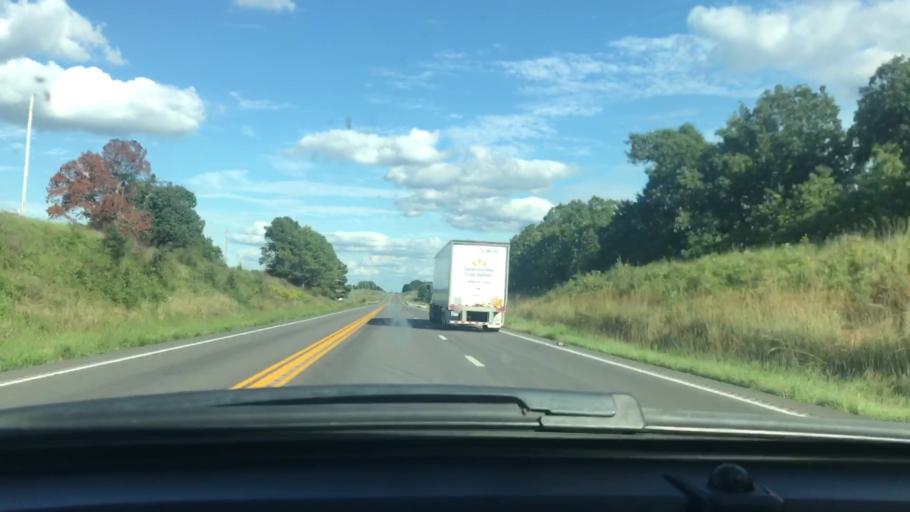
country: US
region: Missouri
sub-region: Oregon County
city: Thayer
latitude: 36.5870
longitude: -91.6294
